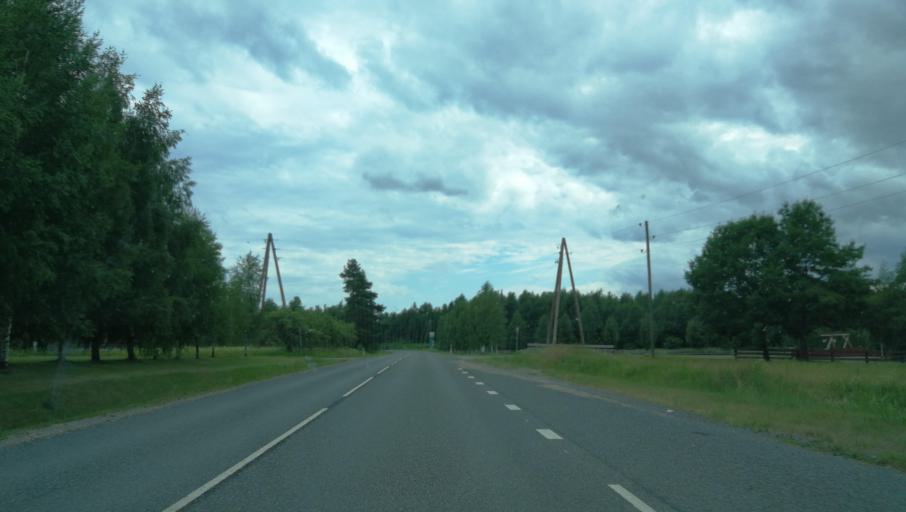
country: LV
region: Naukseni
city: Naukseni
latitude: 57.7294
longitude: 25.4227
